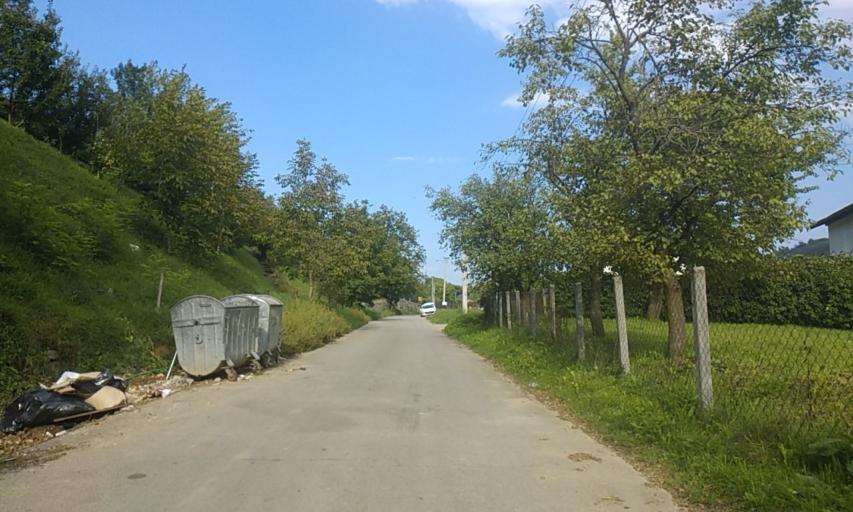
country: BA
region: Republika Srpska
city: Hiseti
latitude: 44.7526
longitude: 17.1678
